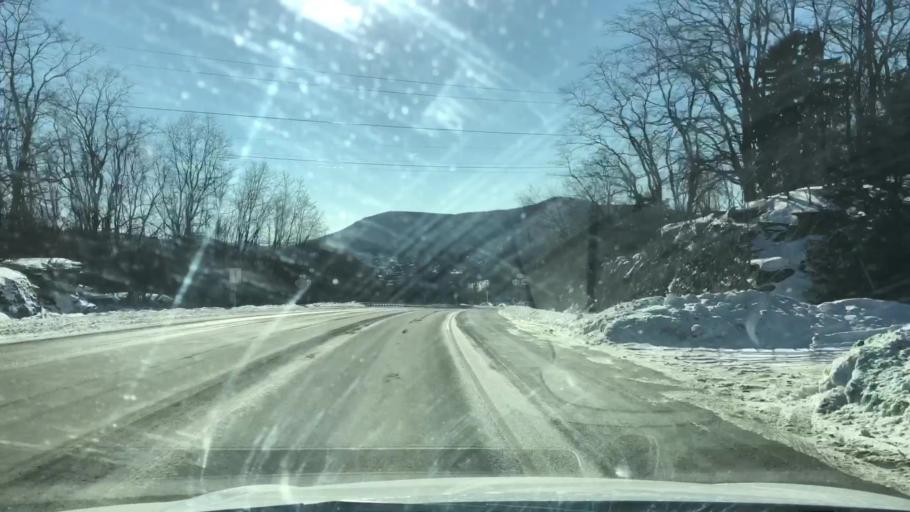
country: US
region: New York
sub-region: Essex County
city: Ticonderoga
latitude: 43.8588
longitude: -73.4136
